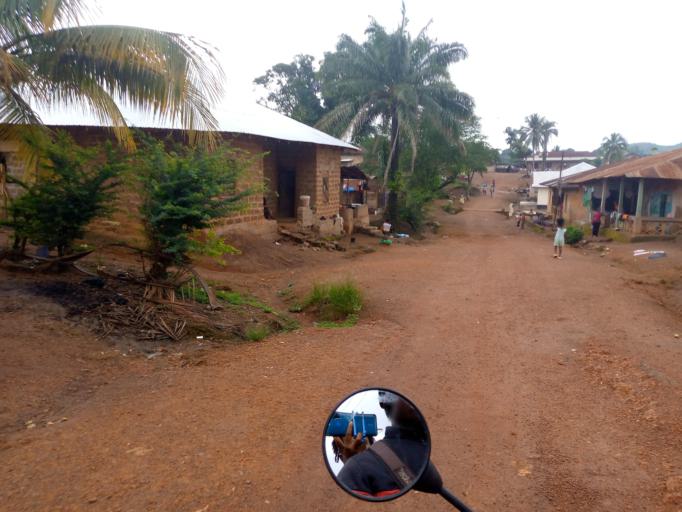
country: SL
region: Eastern Province
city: Kenema
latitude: 7.8648
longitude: -11.1879
